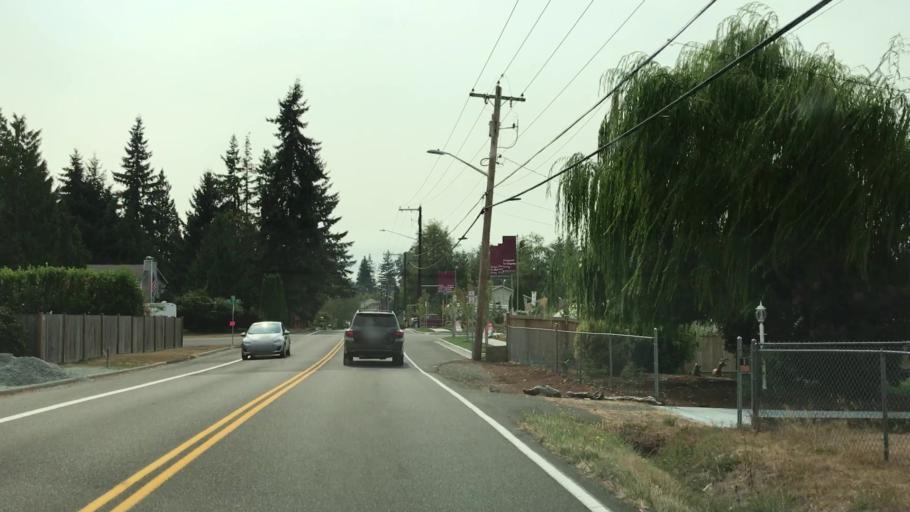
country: US
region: Washington
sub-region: Snohomish County
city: Martha Lake
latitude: 47.8586
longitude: -122.2474
